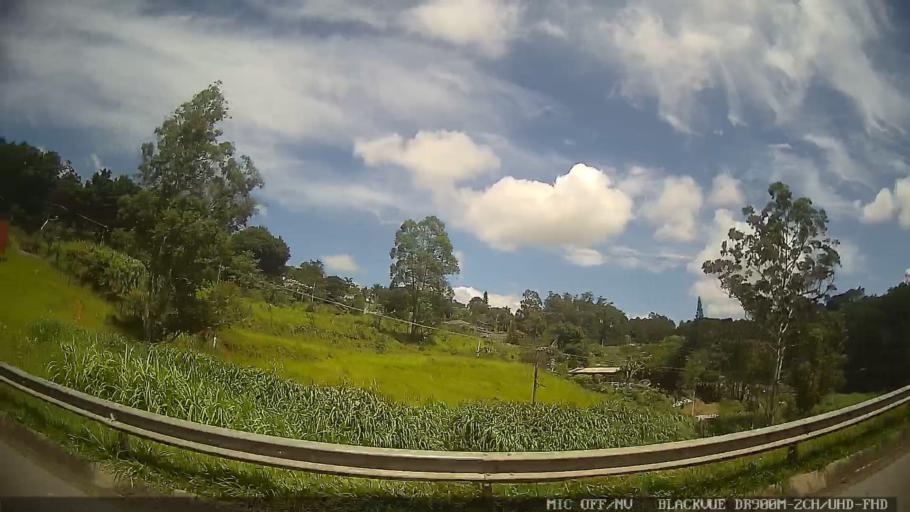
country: BR
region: Sao Paulo
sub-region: Braganca Paulista
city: Braganca Paulista
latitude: -23.0067
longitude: -46.5214
